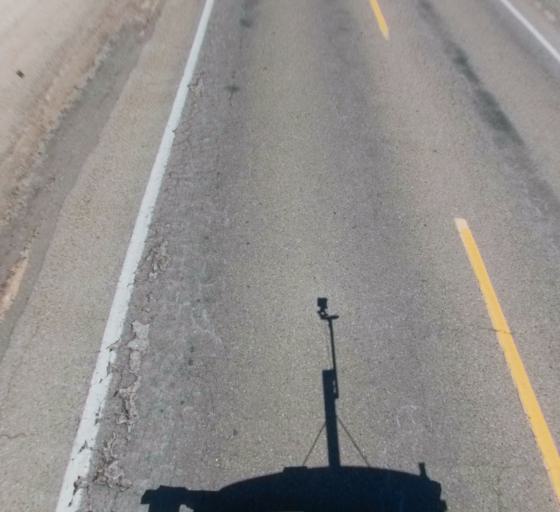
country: US
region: California
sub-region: Fresno County
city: Mendota
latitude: 36.8510
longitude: -120.2673
